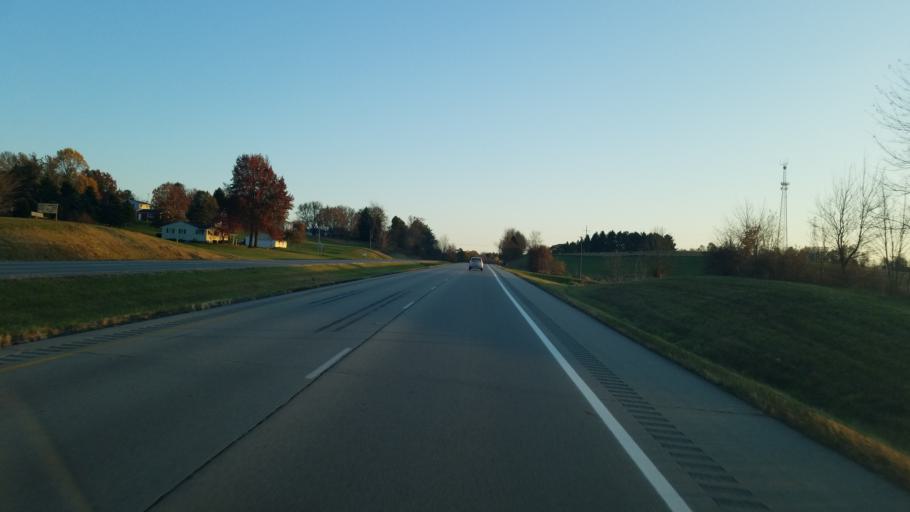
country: US
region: Ohio
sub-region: Sandusky County
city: Bellville
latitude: 40.6584
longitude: -82.5137
